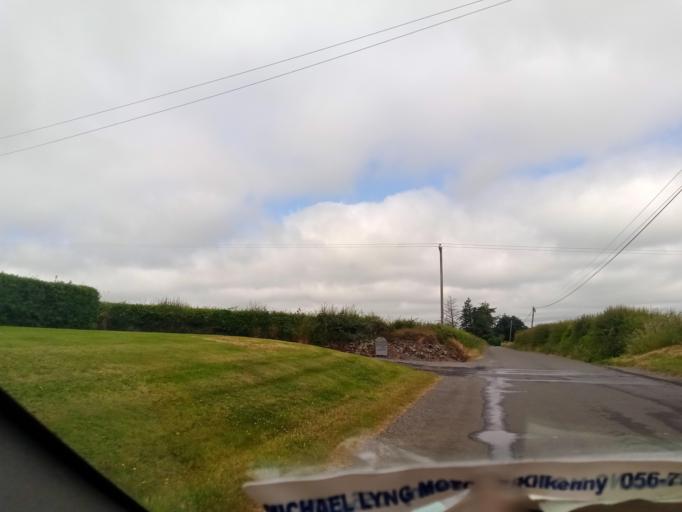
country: IE
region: Leinster
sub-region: Kilkenny
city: Ballyragget
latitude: 52.7566
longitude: -7.4485
